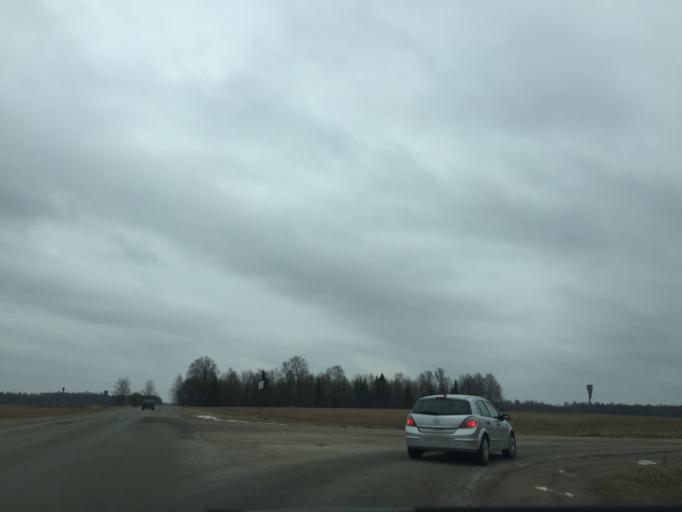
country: LV
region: Kegums
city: Kegums
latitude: 56.7701
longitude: 24.7703
